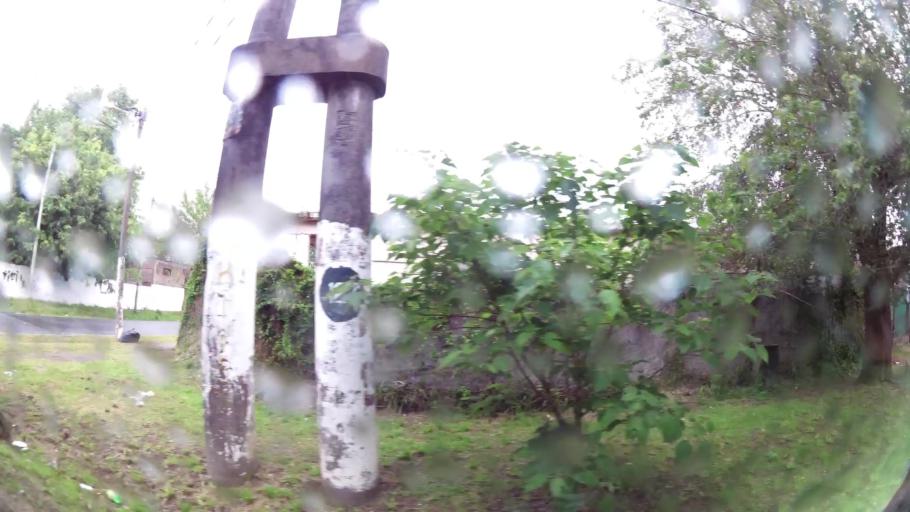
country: AR
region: Buenos Aires
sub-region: Partido de Quilmes
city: Quilmes
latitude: -34.7778
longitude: -58.2296
